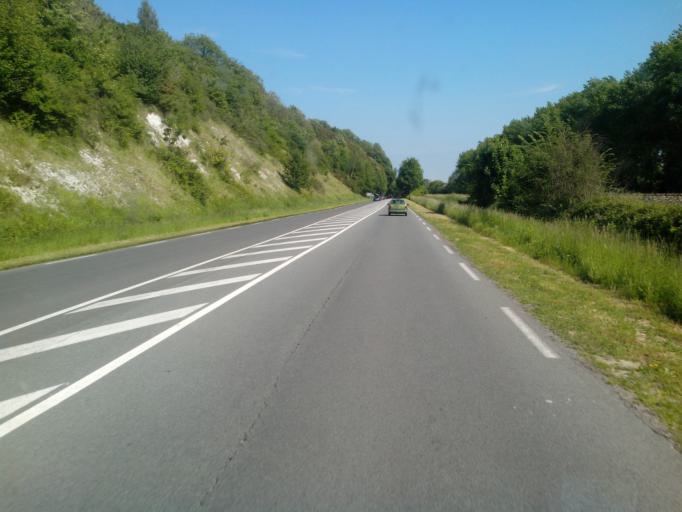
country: FR
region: Picardie
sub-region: Departement de la Somme
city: Sailly-Flibeaucourt
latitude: 50.1314
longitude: 1.7750
